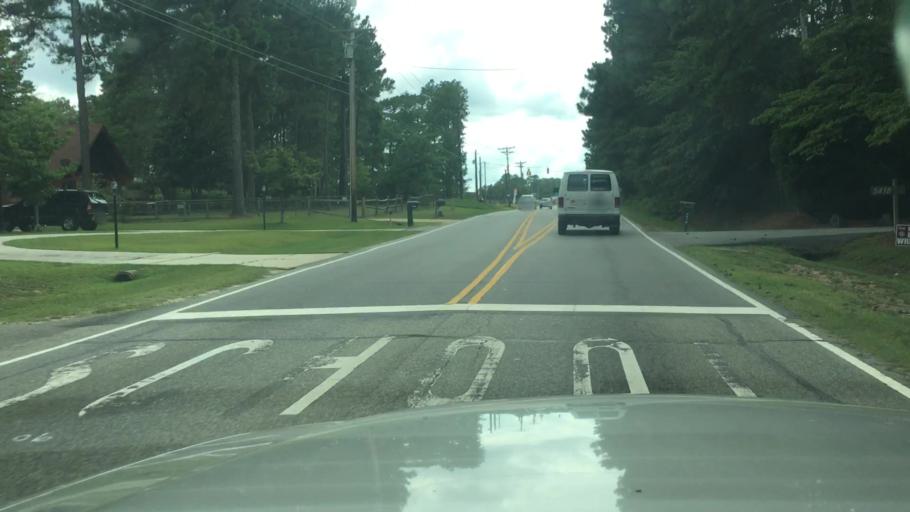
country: US
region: North Carolina
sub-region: Cumberland County
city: Hope Mills
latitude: 35.0012
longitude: -78.9853
